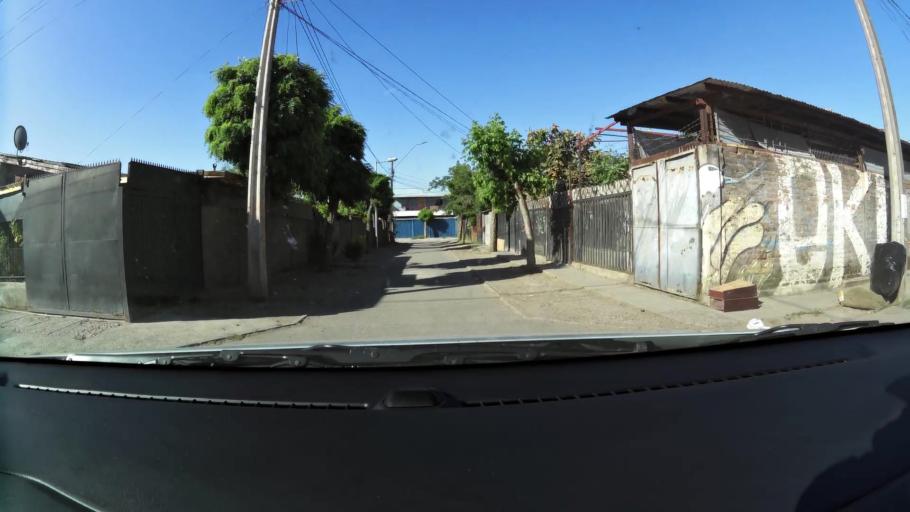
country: CL
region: Santiago Metropolitan
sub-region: Provincia de Maipo
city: San Bernardo
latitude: -33.5898
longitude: -70.6839
